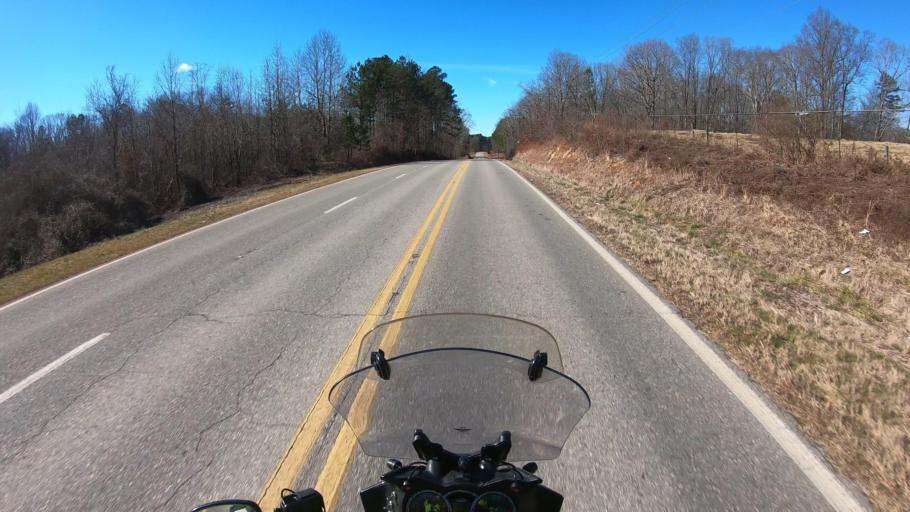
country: US
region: Alabama
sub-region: Cleburne County
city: Heflin
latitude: 33.7285
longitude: -85.4493
